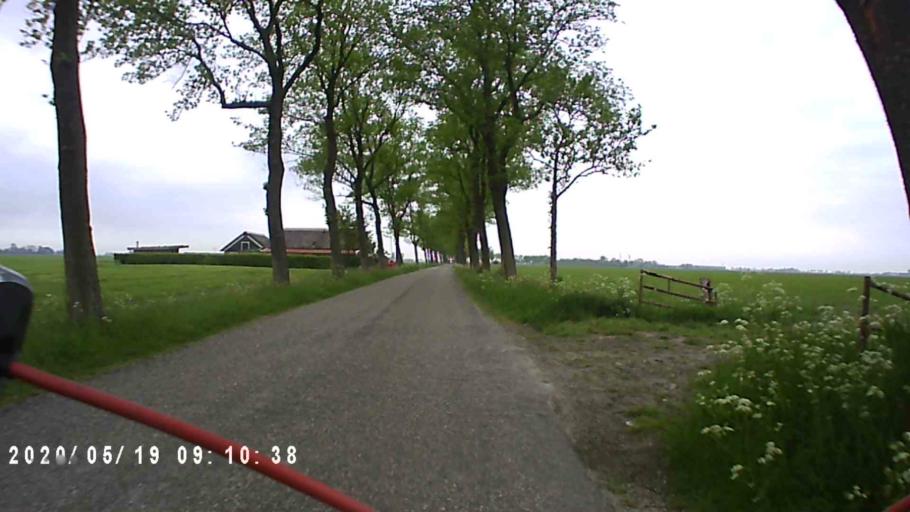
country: NL
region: Groningen
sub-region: Gemeente Zuidhorn
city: Oldehove
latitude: 53.2953
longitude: 6.3875
